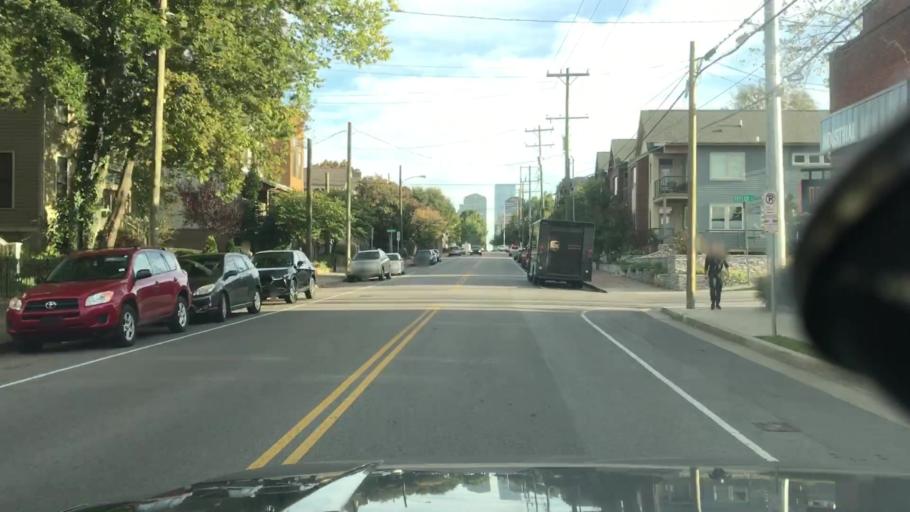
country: US
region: Tennessee
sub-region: Davidson County
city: Nashville
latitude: 36.1788
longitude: -86.7903
